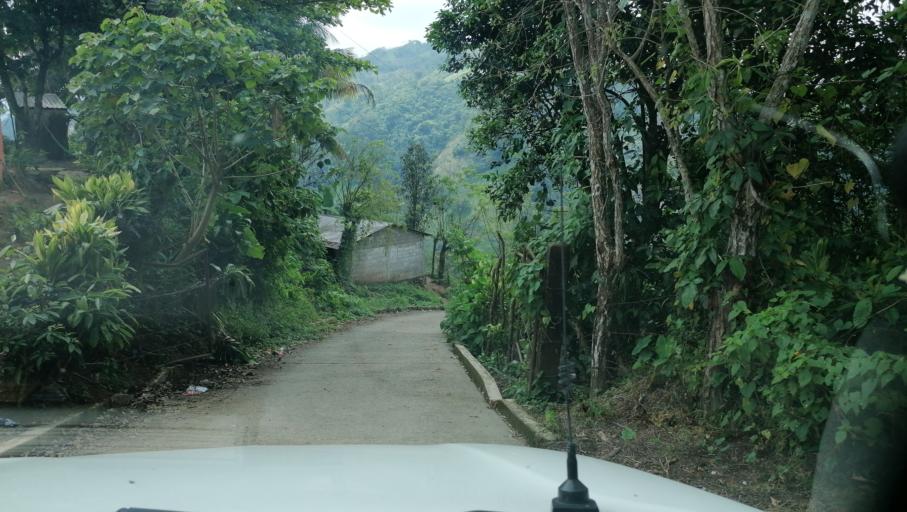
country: MX
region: Chiapas
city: Ixtacomitan
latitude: 17.3575
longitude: -93.1288
